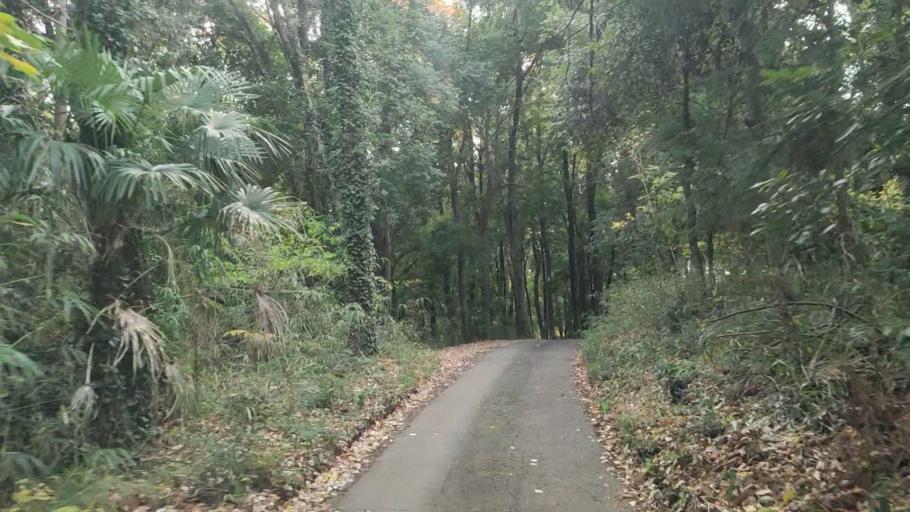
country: JP
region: Kanagawa
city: Minami-rinkan
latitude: 35.4940
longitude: 139.4963
